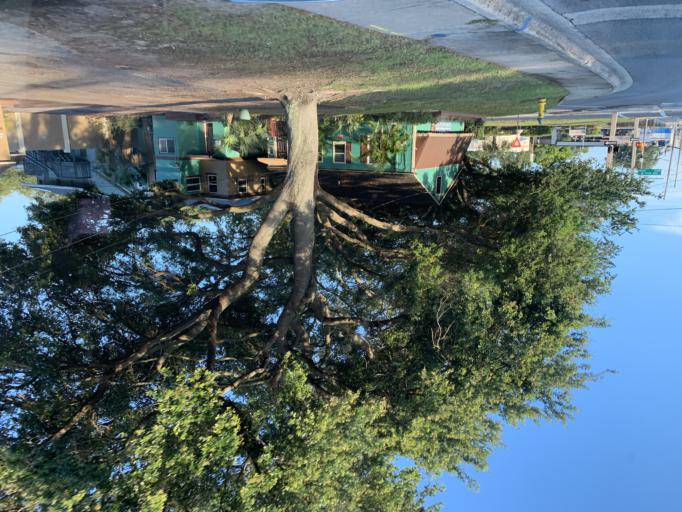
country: US
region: Florida
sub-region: Pinellas County
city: Saint Petersburg
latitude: 27.7725
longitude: -82.6603
